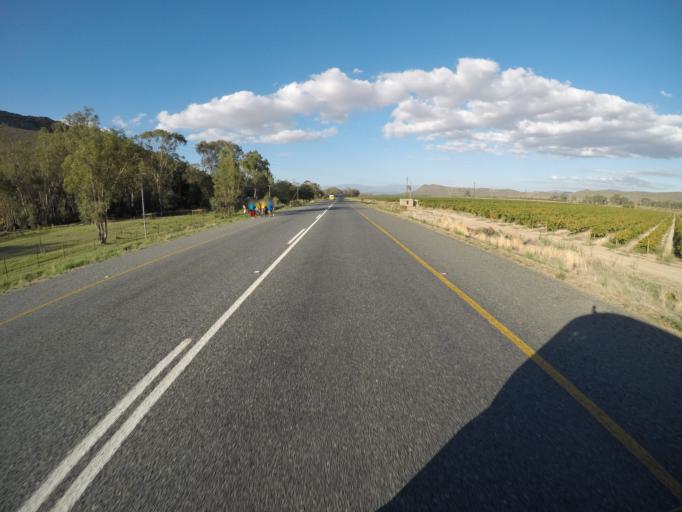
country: ZA
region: Western Cape
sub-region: Cape Winelands District Municipality
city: Worcester
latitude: -33.8177
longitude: 19.4228
